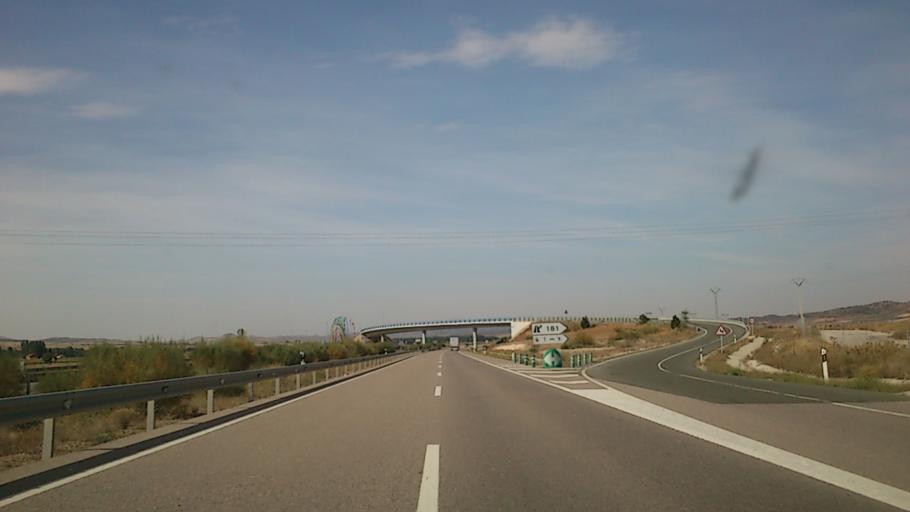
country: ES
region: Aragon
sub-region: Provincia de Teruel
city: Fuentes Claras
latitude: 40.8843
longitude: -1.3059
